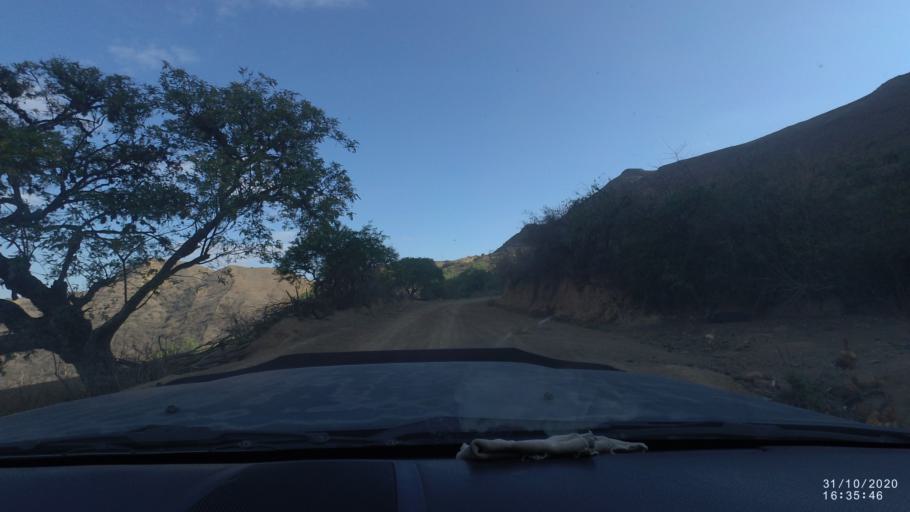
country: BO
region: Chuquisaca
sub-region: Provincia Zudanez
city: Mojocoya
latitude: -18.4551
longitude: -64.5827
